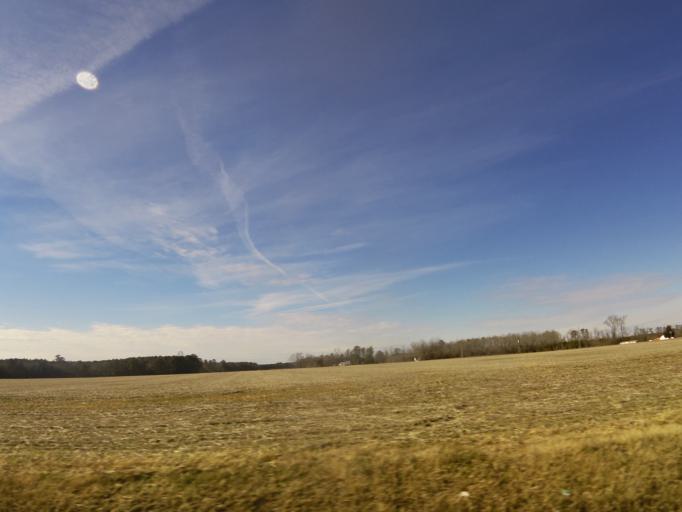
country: US
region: Virginia
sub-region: Isle of Wight County
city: Isle of Wight
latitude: 36.9008
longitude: -76.7162
